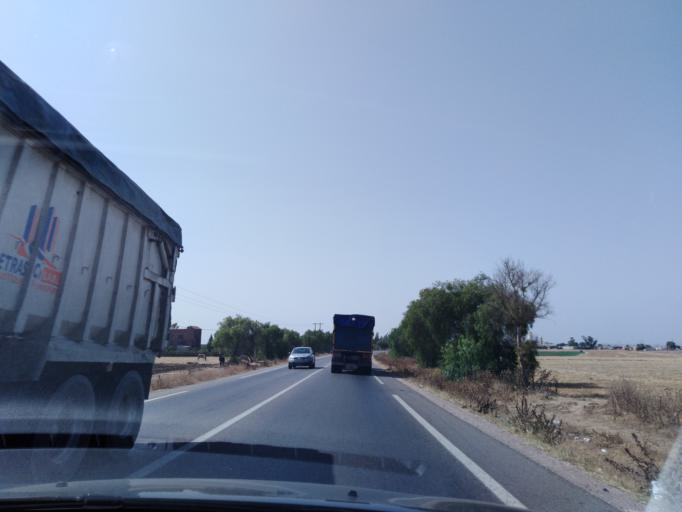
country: MA
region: Chaouia-Ouardigha
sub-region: Settat Province
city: Berrechid
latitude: 33.1818
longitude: -7.6155
